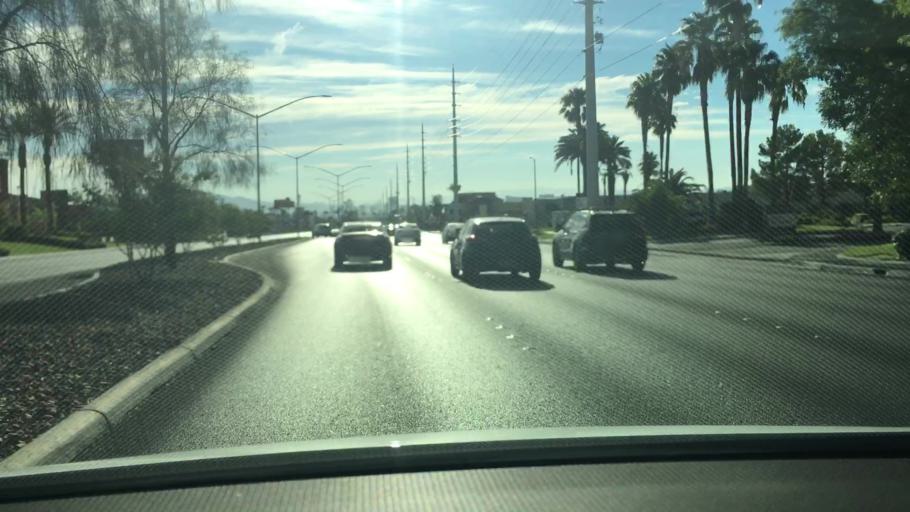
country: US
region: Nevada
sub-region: Clark County
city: Spring Valley
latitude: 36.1439
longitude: -115.2735
